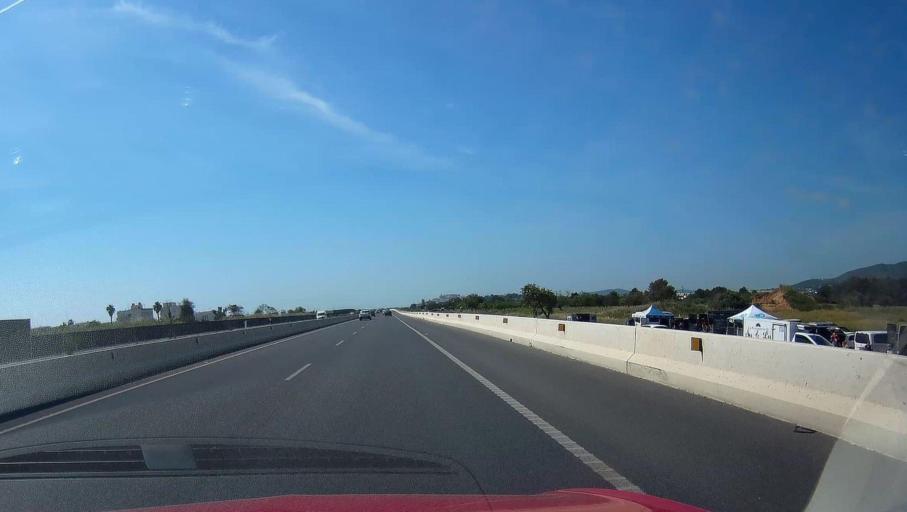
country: ES
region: Balearic Islands
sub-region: Illes Balears
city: Ibiza
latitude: 38.9492
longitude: 1.4434
